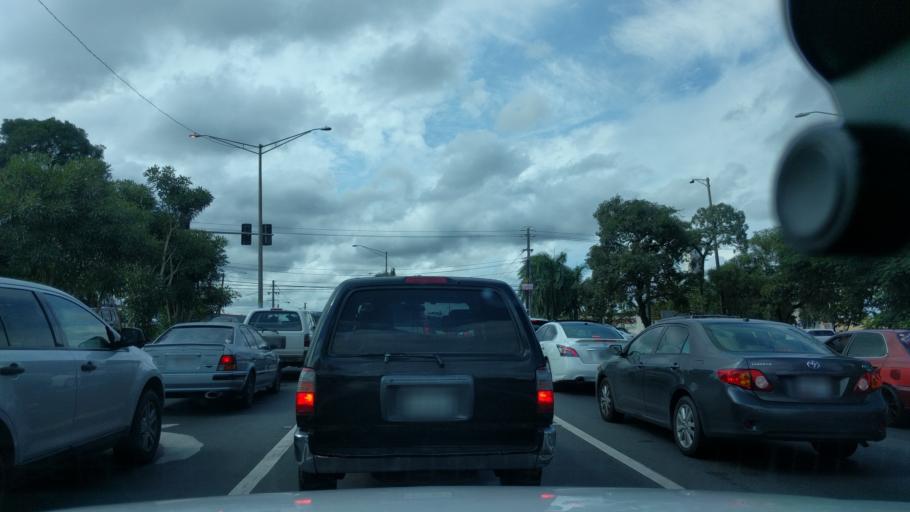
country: PR
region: Toa Alta
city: Pajaros
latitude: 18.3646
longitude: -66.1880
